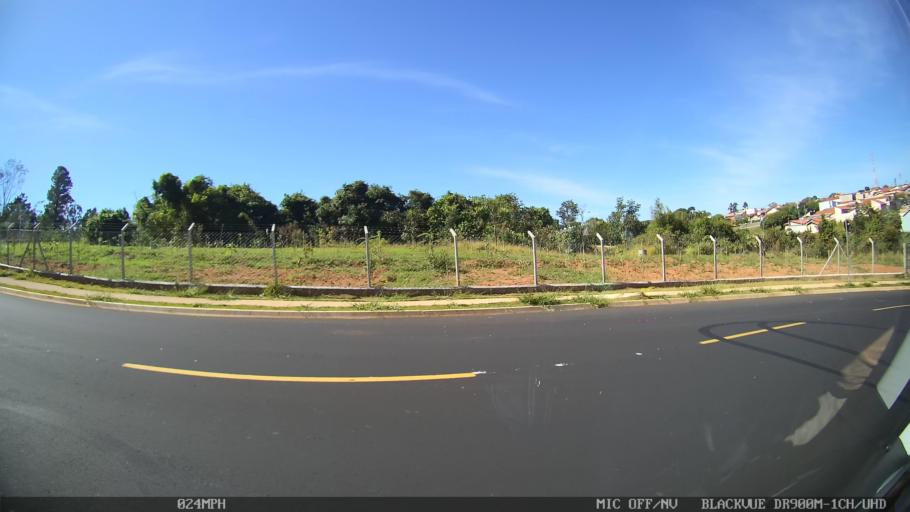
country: BR
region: Sao Paulo
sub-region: Franca
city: Franca
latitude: -20.5540
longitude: -47.3706
